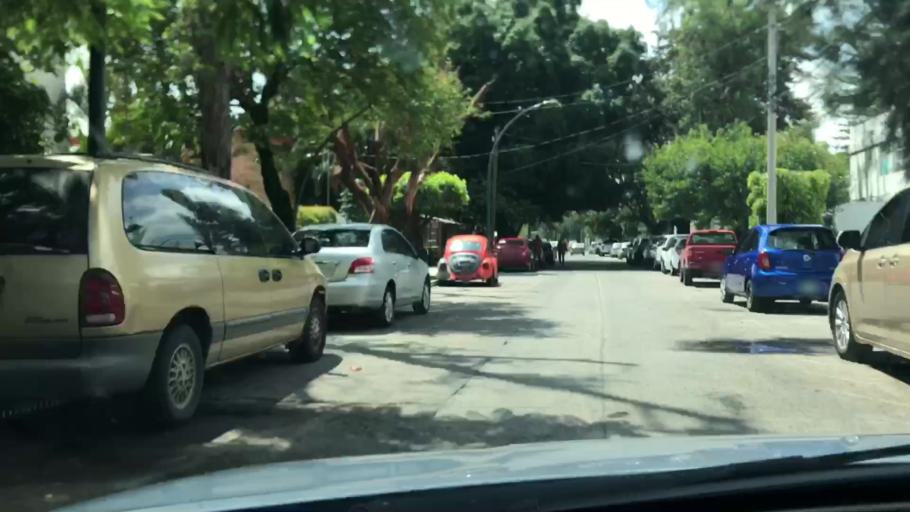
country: MX
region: Jalisco
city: Guadalajara
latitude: 20.6641
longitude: -103.4039
